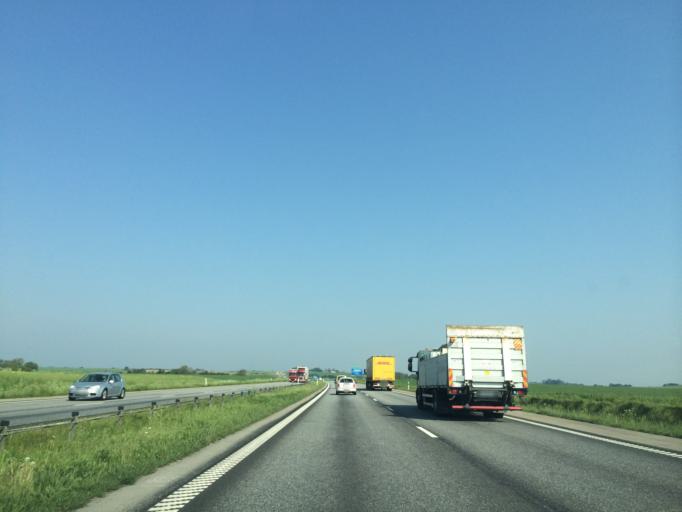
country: SE
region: Skane
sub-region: Landskrona
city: Landskrona
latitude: 55.9127
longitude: 12.8549
